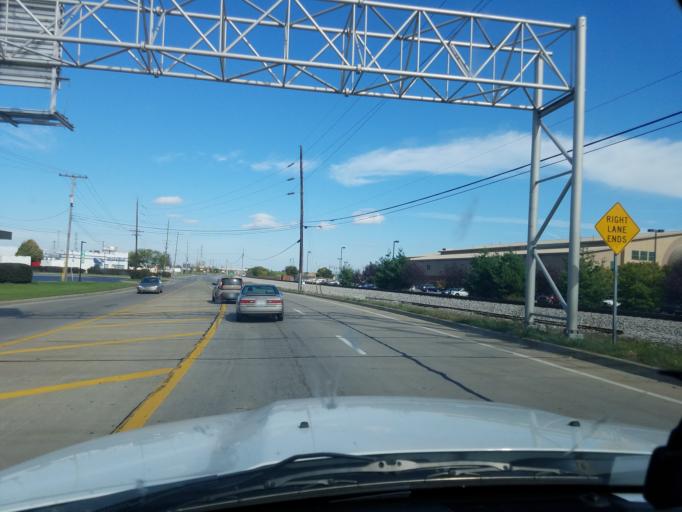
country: US
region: Indiana
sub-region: Clark County
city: Clarksville
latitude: 38.3208
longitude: -85.7515
